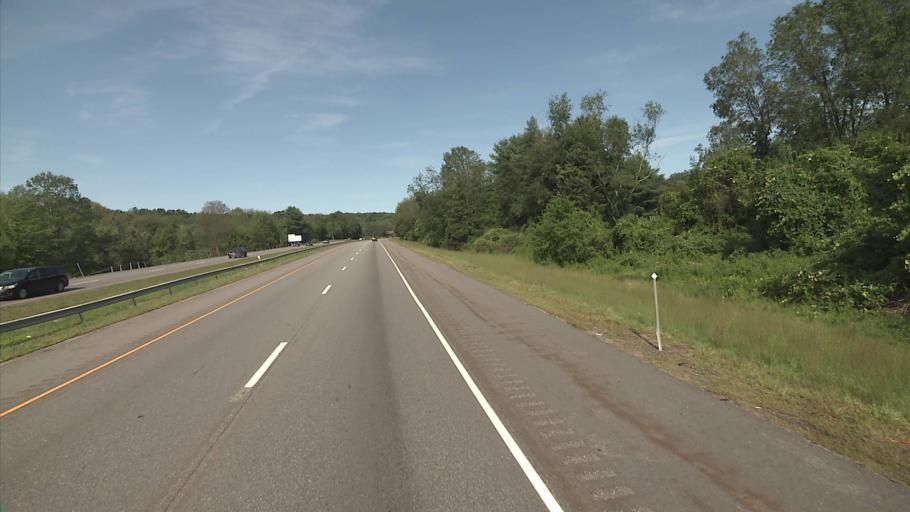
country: US
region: Connecticut
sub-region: New London County
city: Colchester
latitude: 41.5833
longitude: -72.3720
